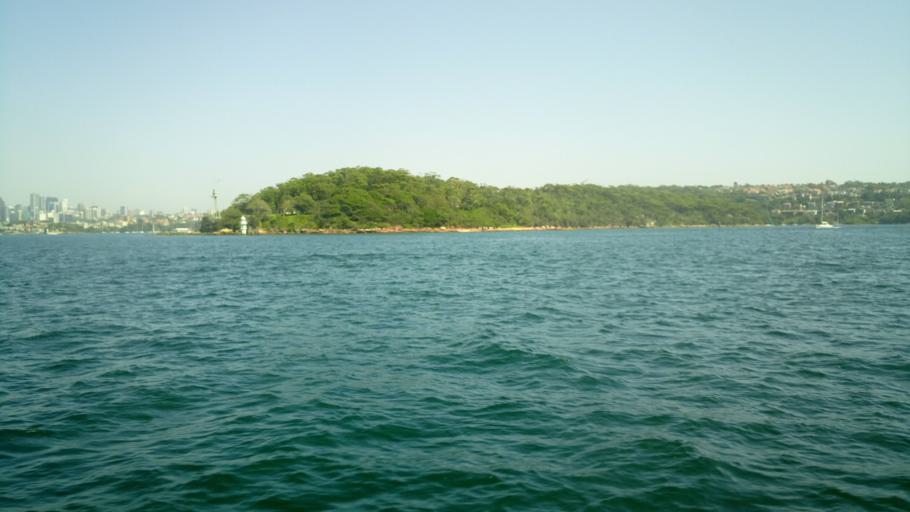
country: AU
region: New South Wales
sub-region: Woollahra
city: Point Piper
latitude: -33.8559
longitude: 151.2503
